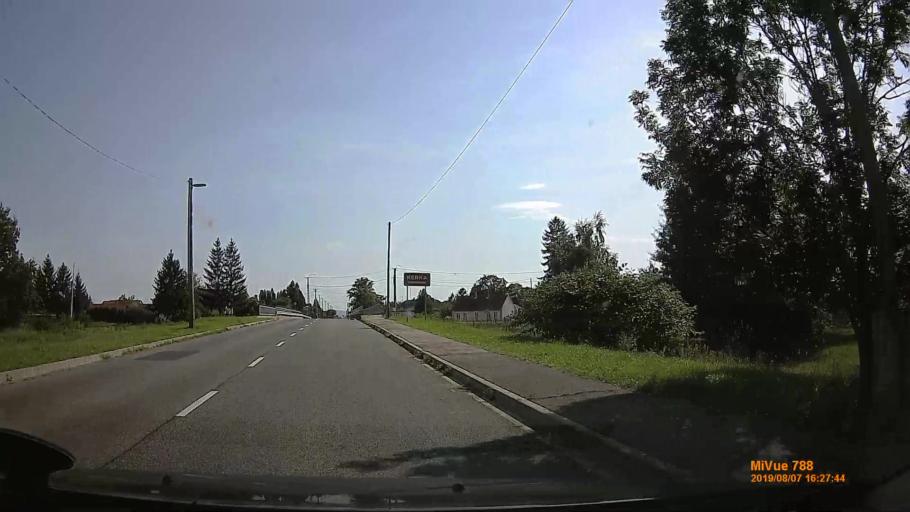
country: HU
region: Zala
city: Lenti
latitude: 46.7002
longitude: 16.5483
